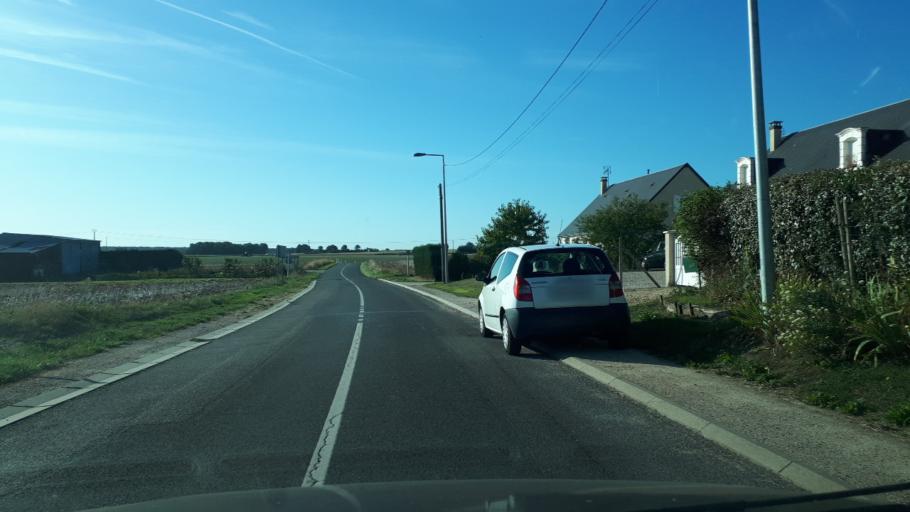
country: FR
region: Centre
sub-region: Departement d'Indre-et-Loire
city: Chateau-Renault
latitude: 47.6456
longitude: 0.9437
